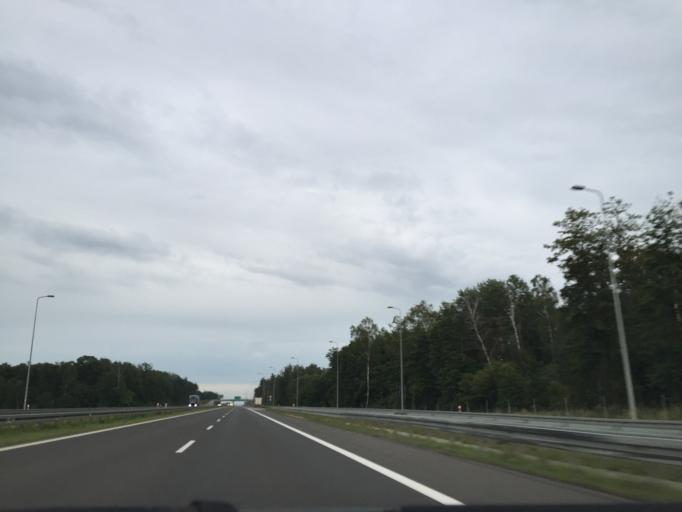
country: PL
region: Podlasie
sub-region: Powiat bialostocki
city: Tykocin
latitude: 53.1369
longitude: 22.7536
